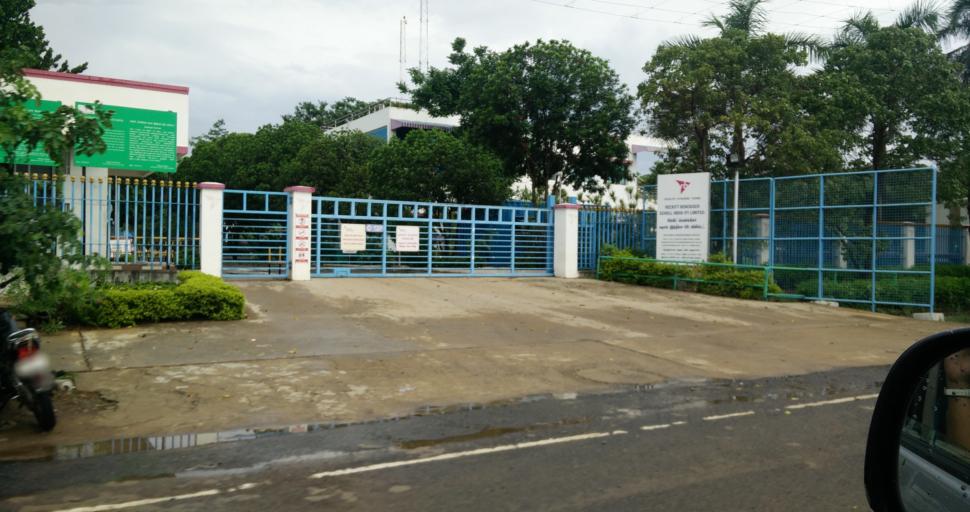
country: IN
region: Tamil Nadu
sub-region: Kancheepuram
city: Nandambakkam
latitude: 12.9995
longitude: 80.0235
